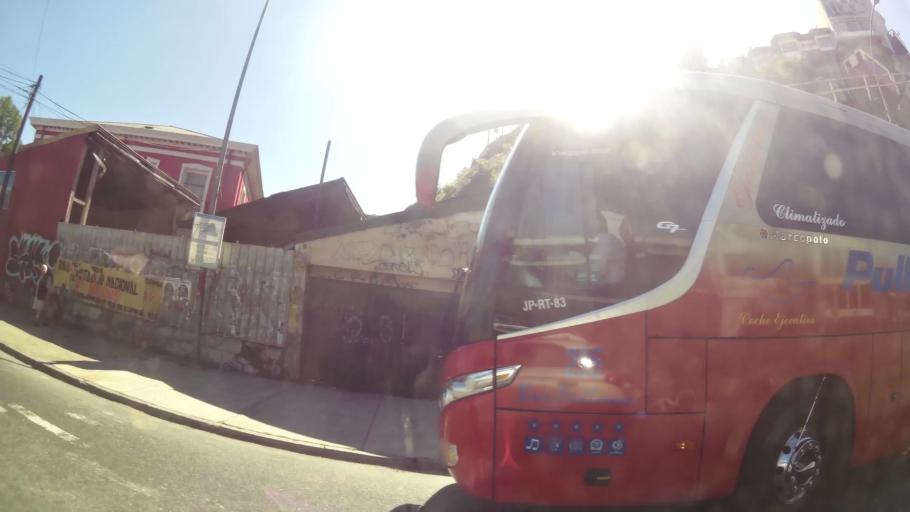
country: CL
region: Valparaiso
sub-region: Provincia de Valparaiso
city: Valparaiso
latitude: -33.0336
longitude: -71.6301
